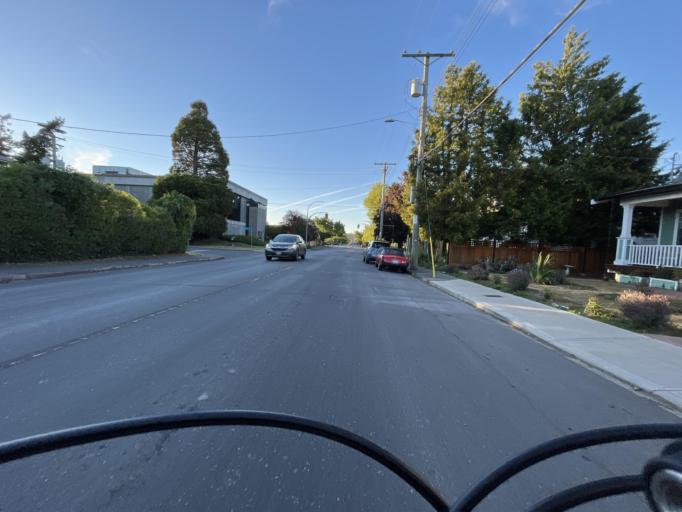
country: CA
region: British Columbia
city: Oak Bay
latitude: 48.4299
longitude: -123.3225
